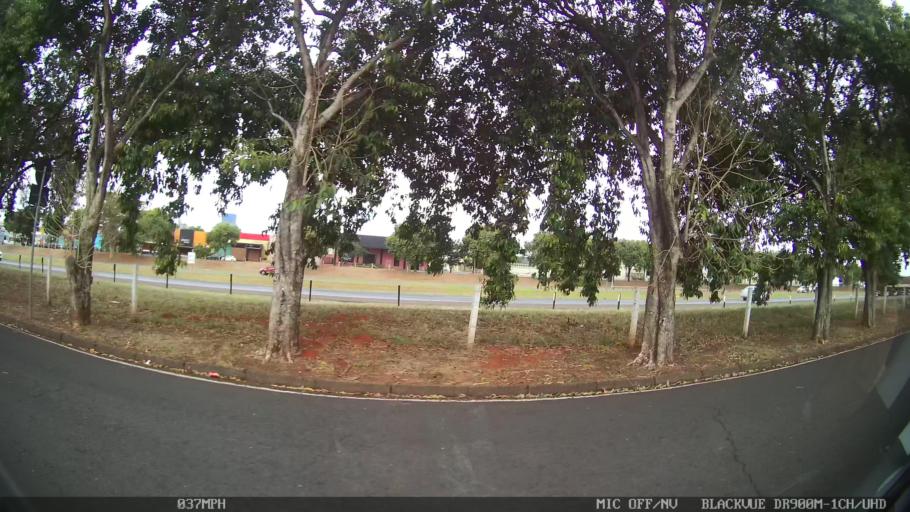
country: BR
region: Sao Paulo
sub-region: Sao Jose Do Rio Preto
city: Sao Jose do Rio Preto
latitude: -20.8240
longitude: -49.4113
